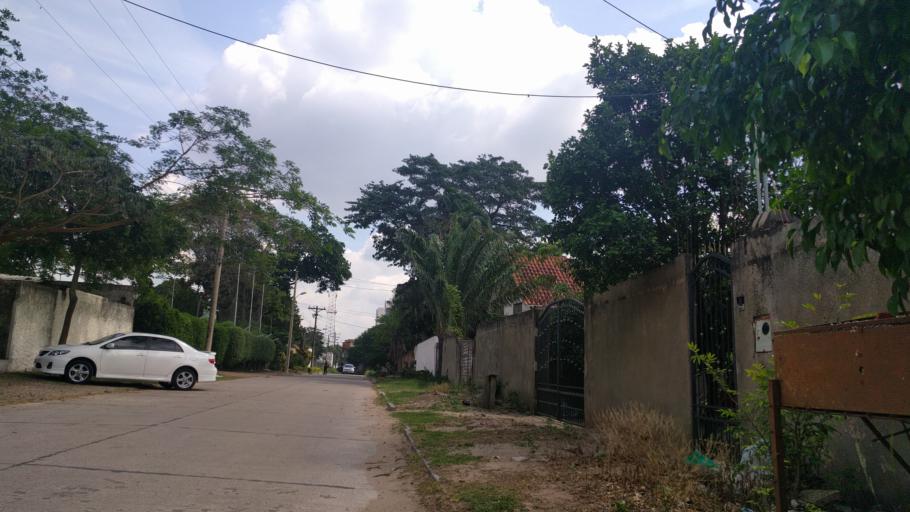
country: BO
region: Santa Cruz
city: Santa Cruz de la Sierra
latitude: -17.7915
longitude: -63.2227
